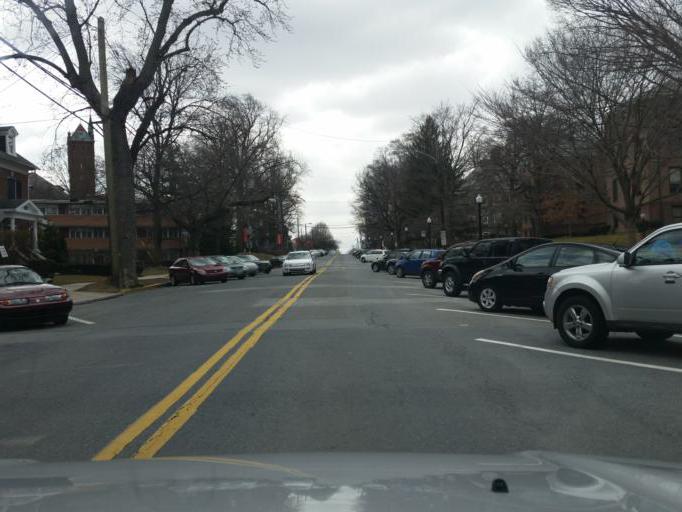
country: US
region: Pennsylvania
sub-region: Lancaster County
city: Lancaster
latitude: 40.0470
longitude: -76.3184
